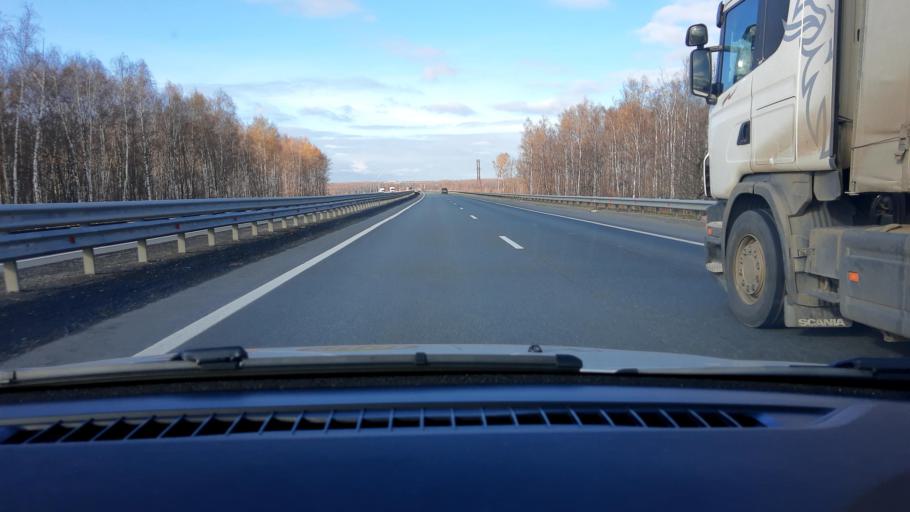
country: RU
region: Nizjnij Novgorod
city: Burevestnik
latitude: 56.1189
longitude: 43.8168
